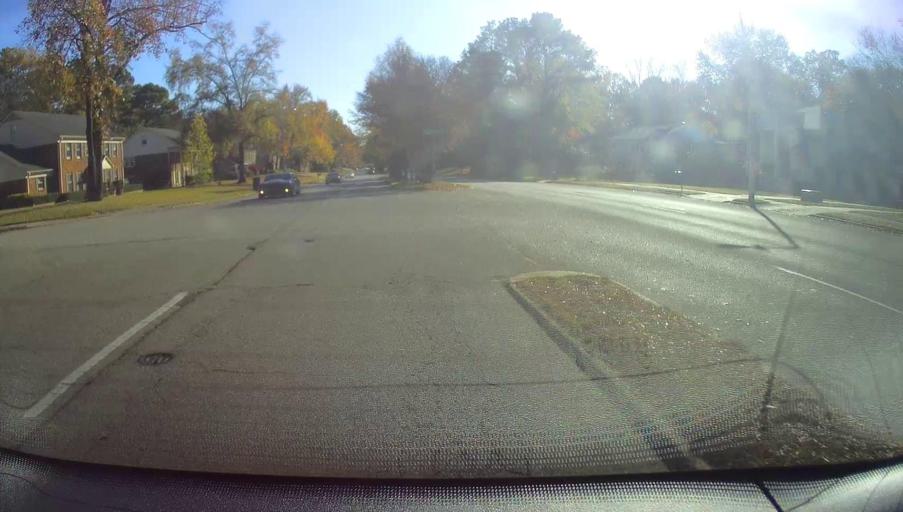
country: US
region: Tennessee
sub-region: Shelby County
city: Germantown
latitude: 35.0873
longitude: -89.8403
